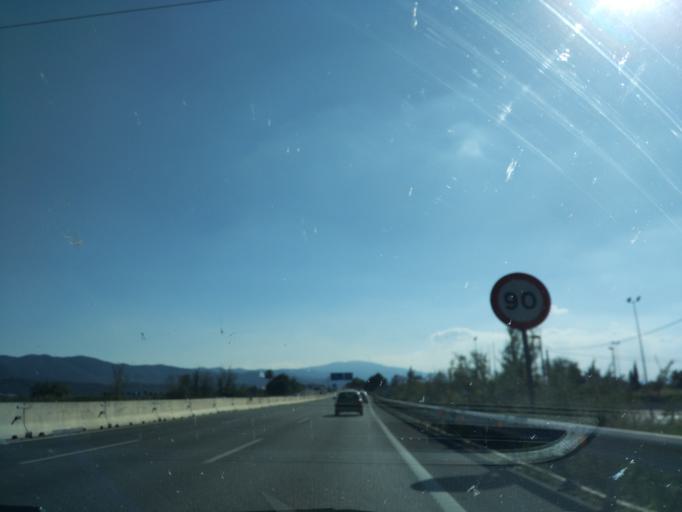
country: ES
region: Murcia
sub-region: Murcia
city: Murcia
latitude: 37.9522
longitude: -1.1417
